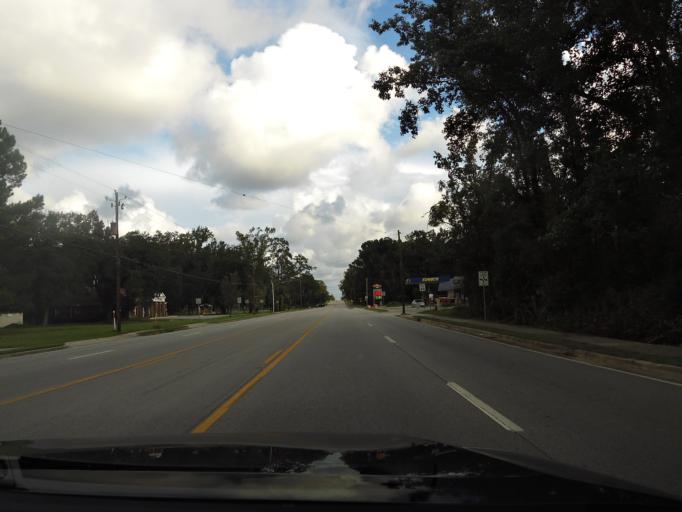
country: US
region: Georgia
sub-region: Liberty County
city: Midway
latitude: 31.7402
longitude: -81.4380
